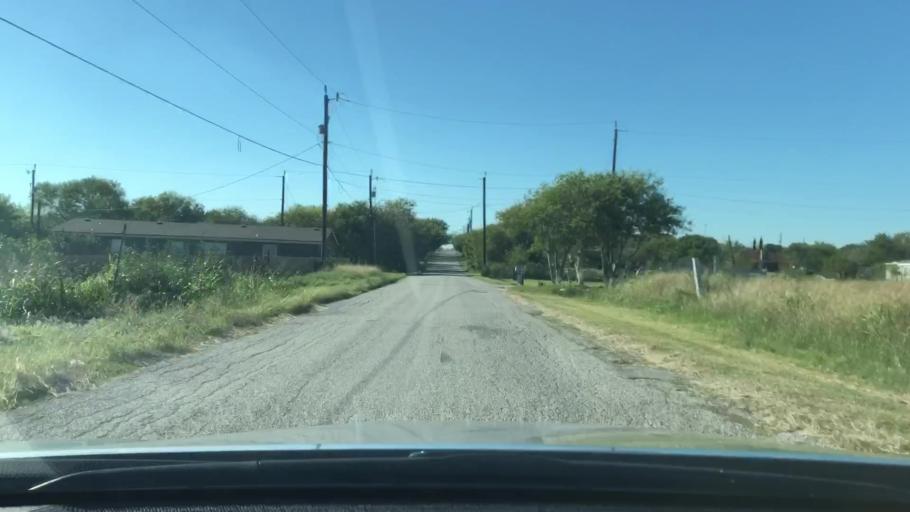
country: US
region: Texas
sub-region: Bexar County
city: Converse
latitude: 29.4678
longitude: -98.3019
